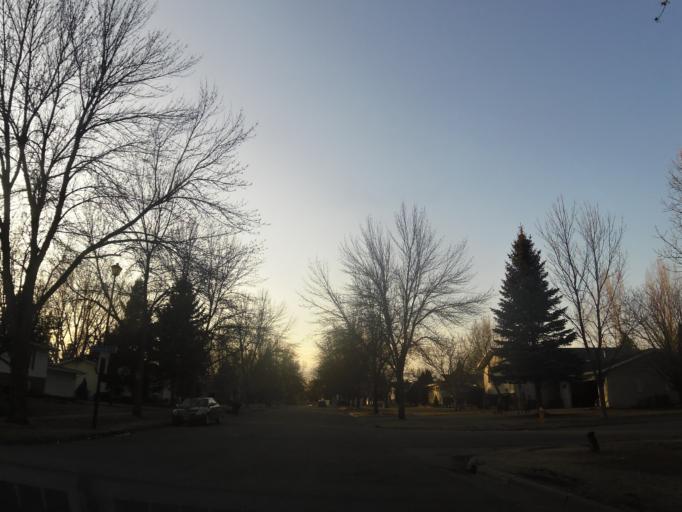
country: US
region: North Dakota
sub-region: Grand Forks County
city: Grand Forks
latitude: 47.8795
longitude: -97.0250
